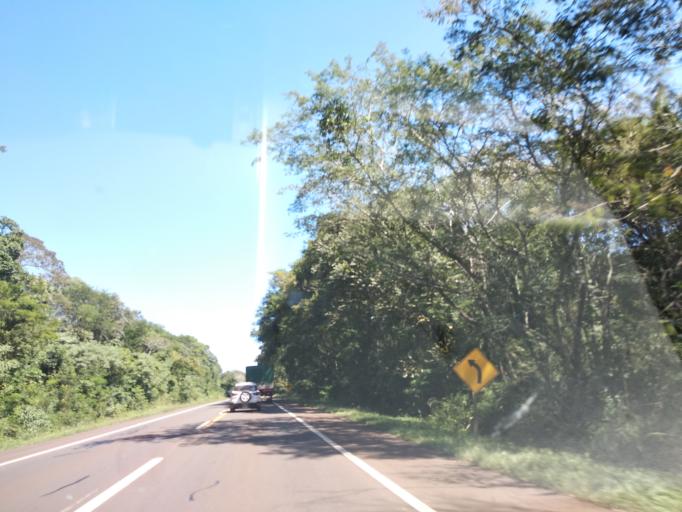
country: AR
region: Misiones
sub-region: Departamento de Iguazu
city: Puerto Iguazu
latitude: -25.6878
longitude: -54.5129
